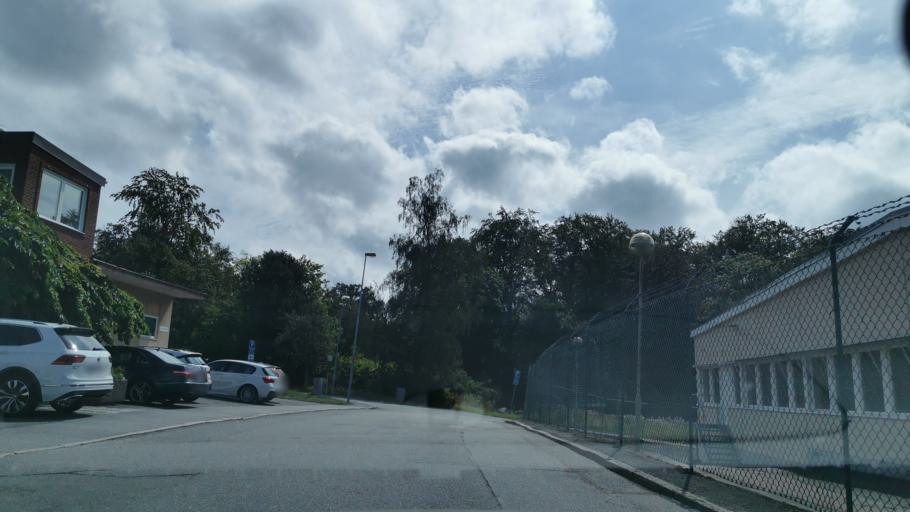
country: SE
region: Vaestra Goetaland
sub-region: Molndal
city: Moelndal
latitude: 57.6670
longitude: 12.0210
